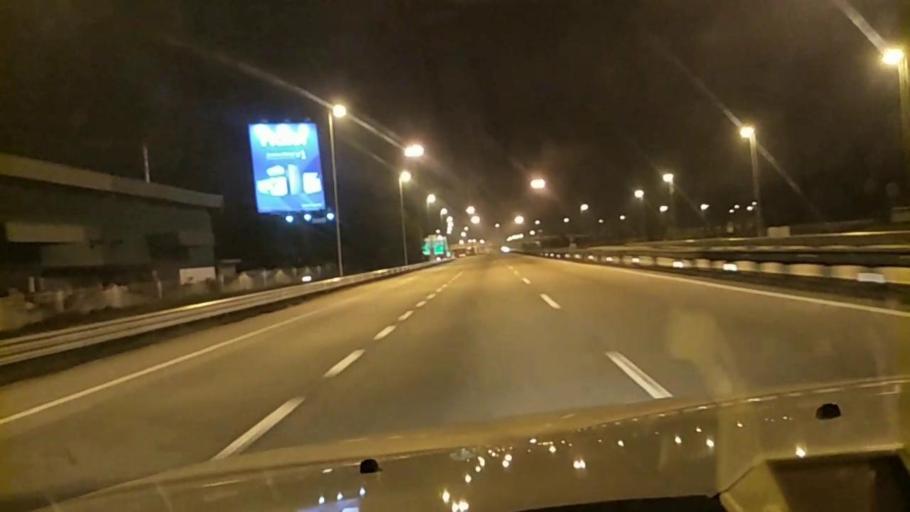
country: MY
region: Penang
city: Juru
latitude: 5.2467
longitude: 100.4730
